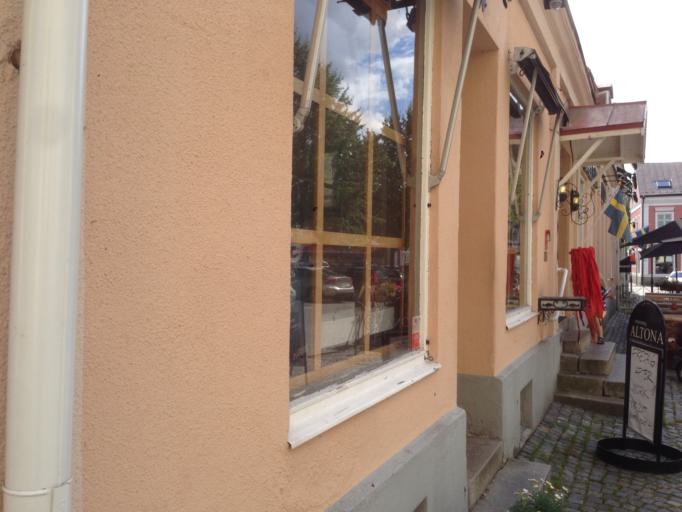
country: SE
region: Blekinge
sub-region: Solvesborgs Kommun
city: Soelvesborg
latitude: 56.0524
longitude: 14.5876
